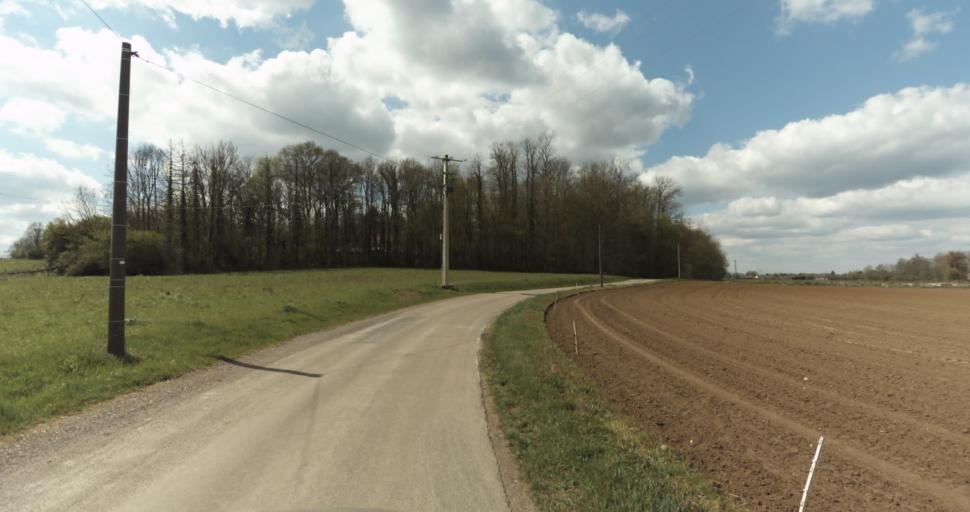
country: FR
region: Bourgogne
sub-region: Departement de la Cote-d'Or
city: Auxonne
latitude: 47.1869
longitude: 5.4180
